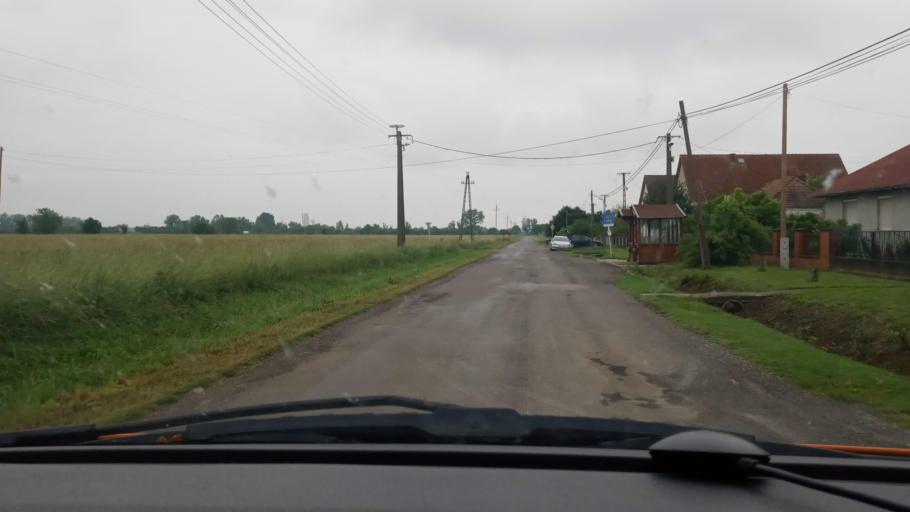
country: HU
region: Baranya
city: Szentlorinc
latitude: 46.0473
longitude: 17.9682
